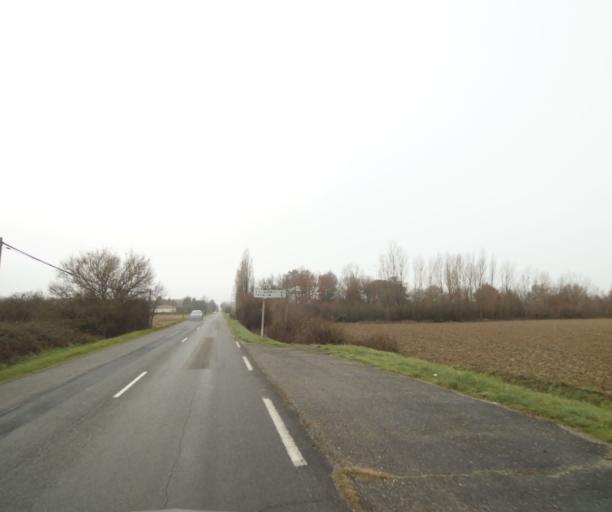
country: FR
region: Midi-Pyrenees
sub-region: Departement de la Haute-Garonne
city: Villemur-sur-Tarn
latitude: 43.8531
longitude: 1.4717
